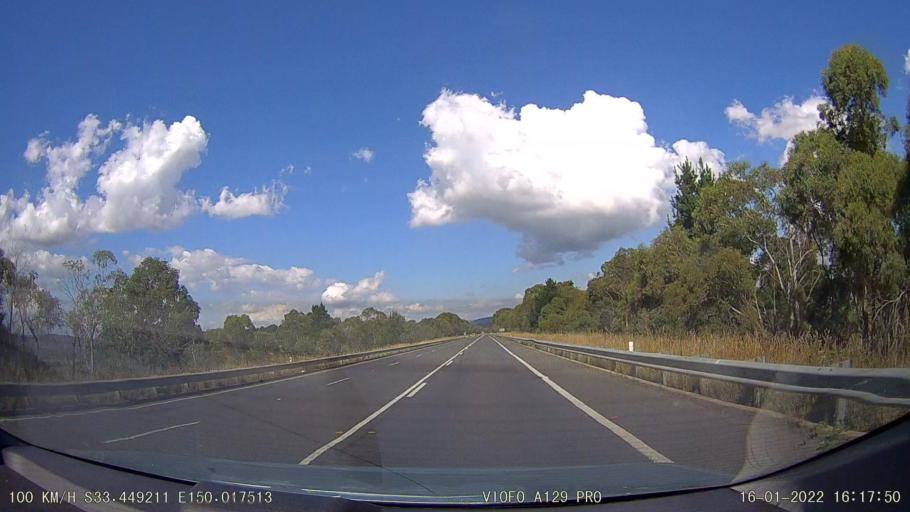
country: AU
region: New South Wales
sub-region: Lithgow
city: Portland
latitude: -33.4495
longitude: 150.0171
